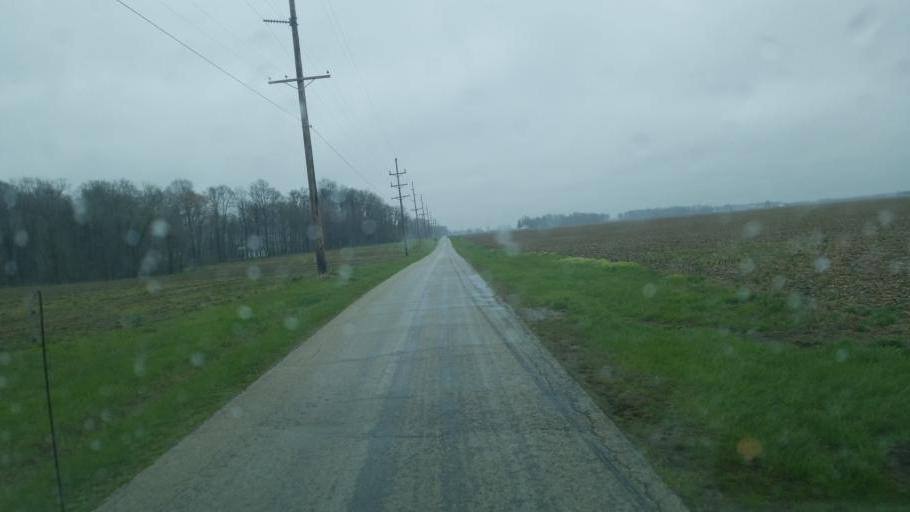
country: US
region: Ohio
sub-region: Crawford County
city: Bucyrus
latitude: 40.8338
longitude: -83.0910
